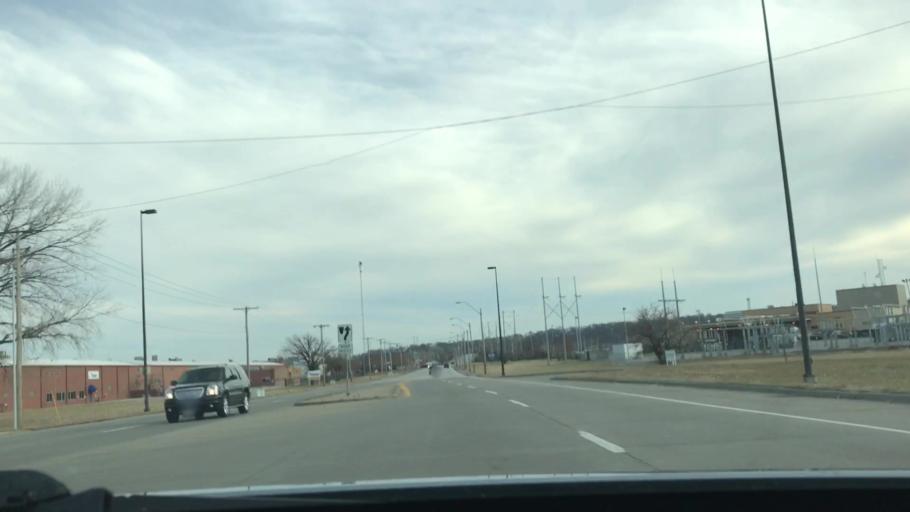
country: US
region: Missouri
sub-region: Clay County
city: North Kansas City
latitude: 39.1360
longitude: -94.5275
